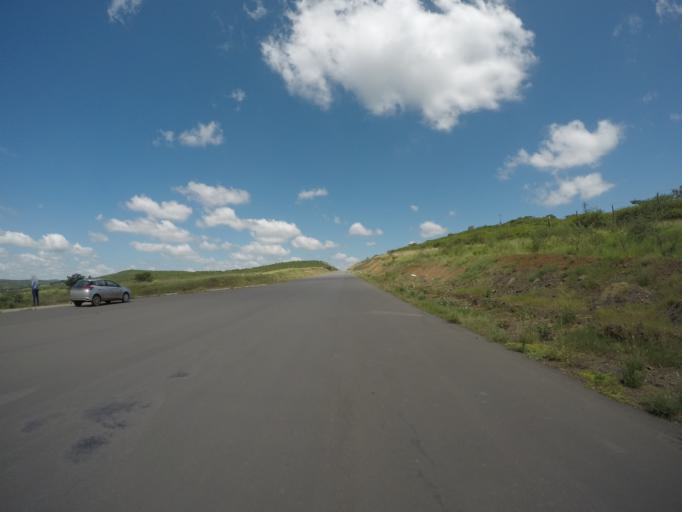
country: ZA
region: KwaZulu-Natal
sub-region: uThungulu District Municipality
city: Empangeni
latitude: -28.6206
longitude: 31.7565
